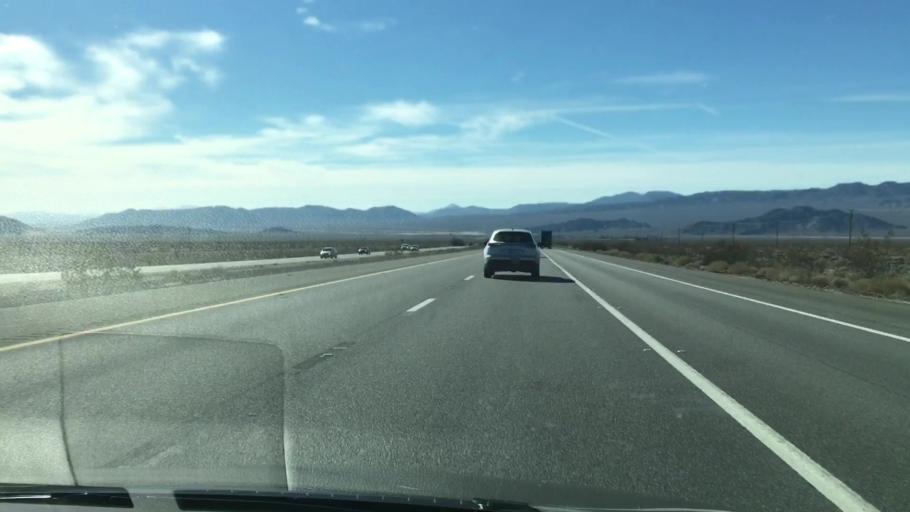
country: US
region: Nevada
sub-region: Clark County
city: Sandy Valley
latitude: 35.3073
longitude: -116.0093
